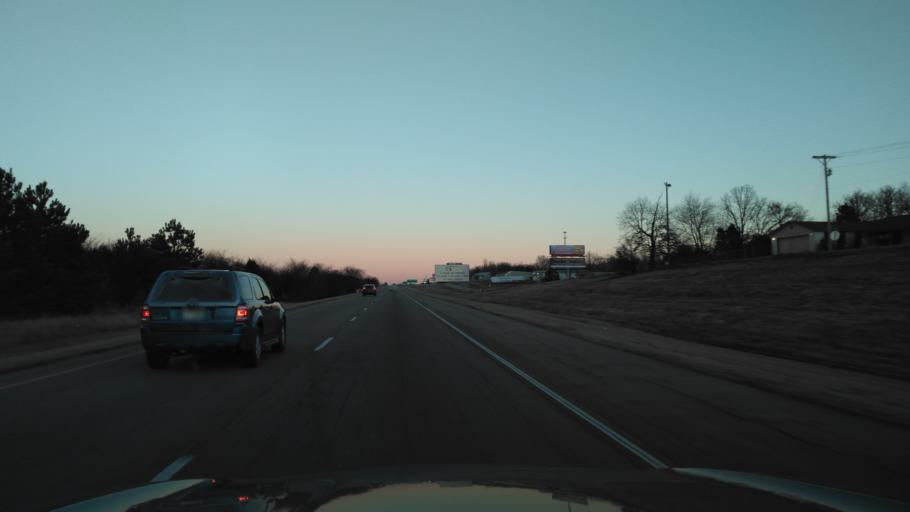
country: US
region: Arkansas
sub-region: Crawford County
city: Van Buren
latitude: 35.4645
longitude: -94.3711
